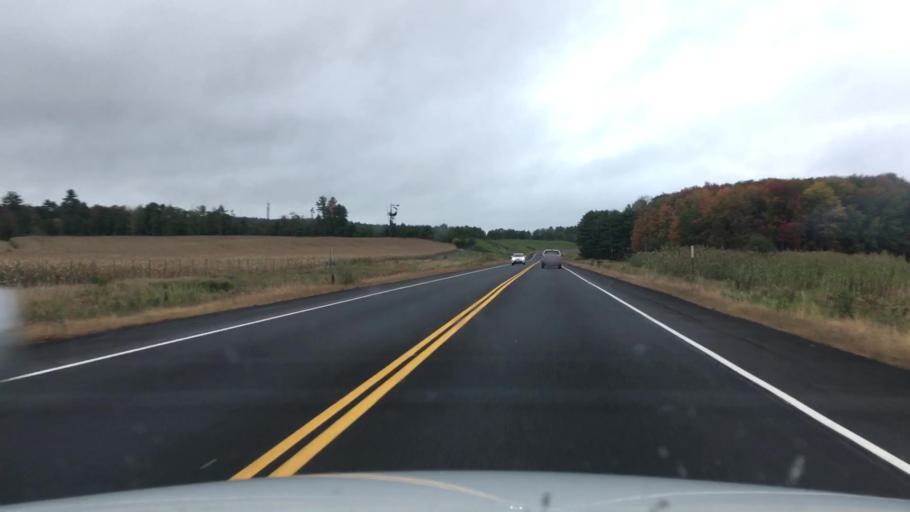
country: US
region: Maine
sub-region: Cumberland County
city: New Gloucester
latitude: 43.8898
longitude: -70.3423
